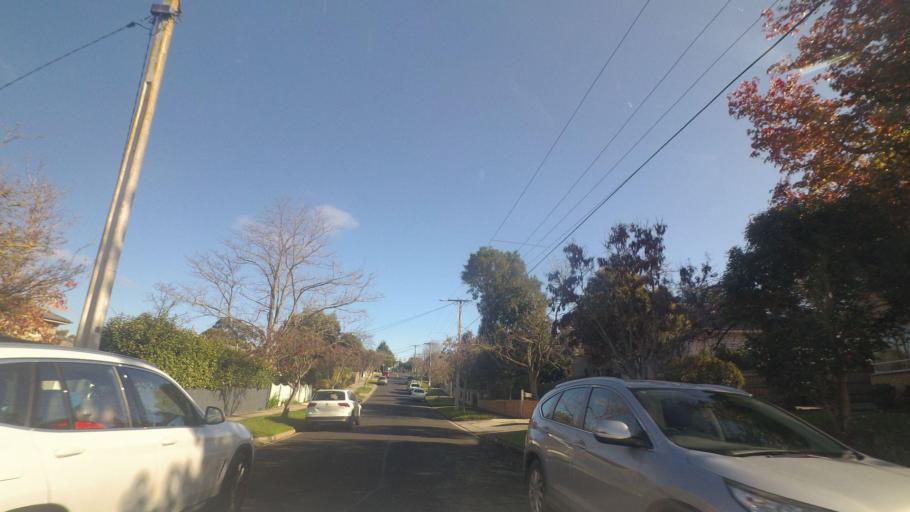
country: AU
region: Victoria
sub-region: Whitehorse
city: Mont Albert North
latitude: -37.8013
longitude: 145.1145
